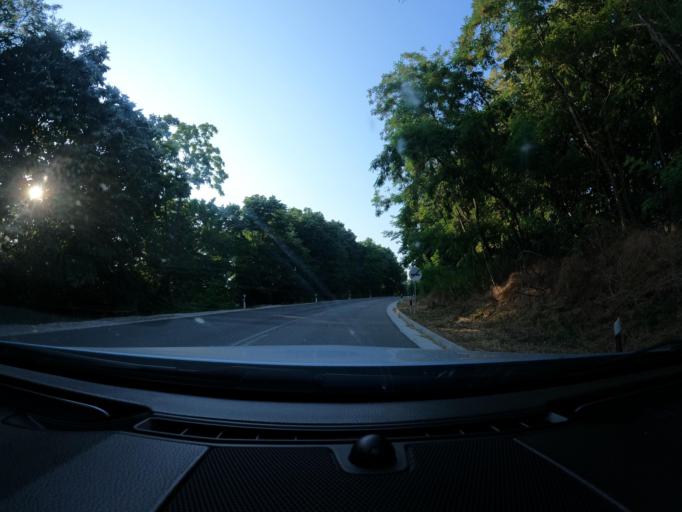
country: RS
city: Vrdnik
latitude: 45.1307
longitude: 19.7246
